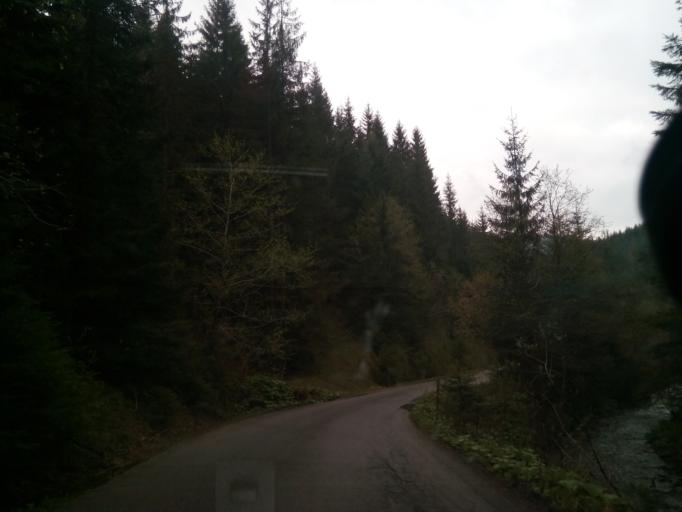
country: SK
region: Zilinsky
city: Oravska Lesna
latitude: 49.3035
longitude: 19.2058
